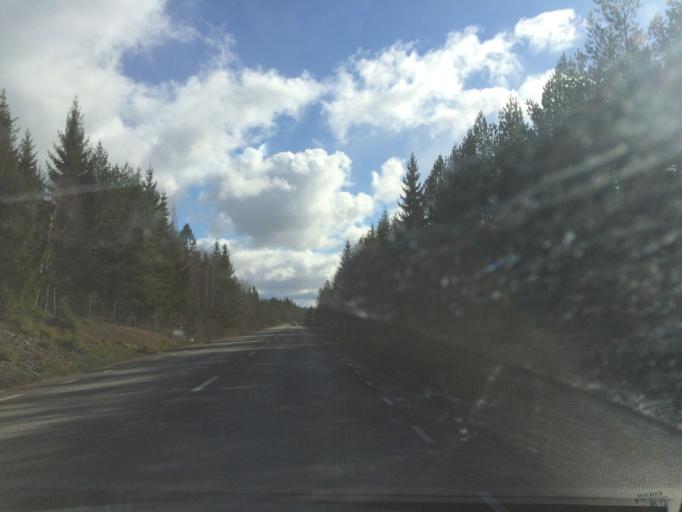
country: SE
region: Vaestra Goetaland
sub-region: Skara Kommun
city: Skara
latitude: 58.3606
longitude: 13.4235
